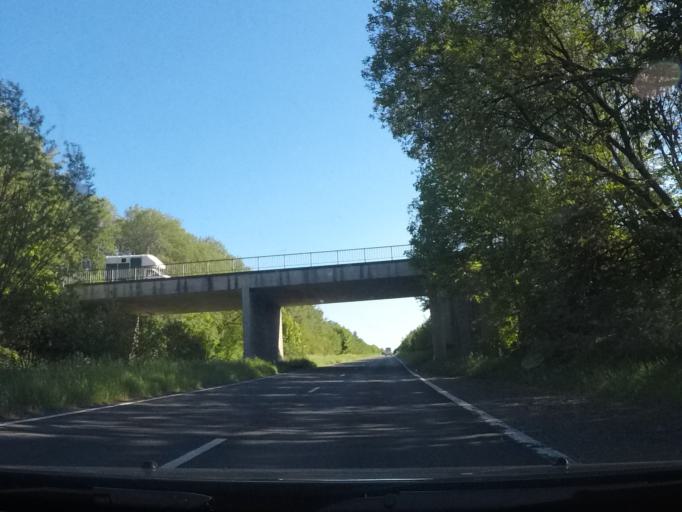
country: BE
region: Wallonia
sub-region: Province du Luxembourg
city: Saint-Hubert
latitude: 49.9888
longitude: 5.3796
